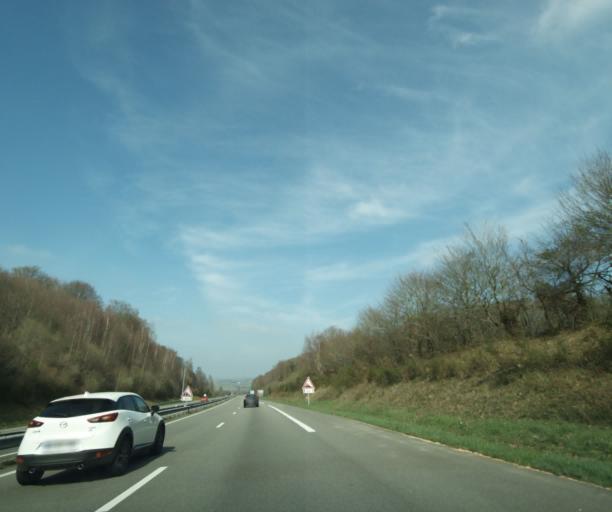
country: FR
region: Limousin
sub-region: Departement de la Haute-Vienne
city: Bessines-sur-Gartempe
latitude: 46.0900
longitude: 1.3624
